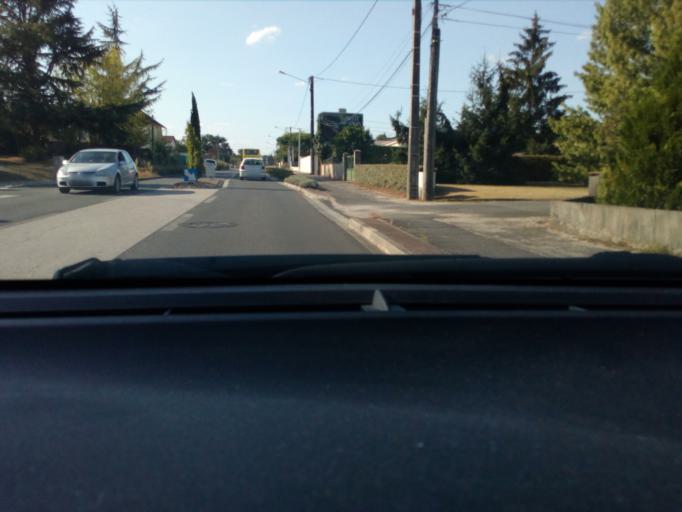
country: FR
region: Poitou-Charentes
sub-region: Departement de la Charente
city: Saint-Yrieix-sur-Charente
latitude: 45.6762
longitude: 0.1220
